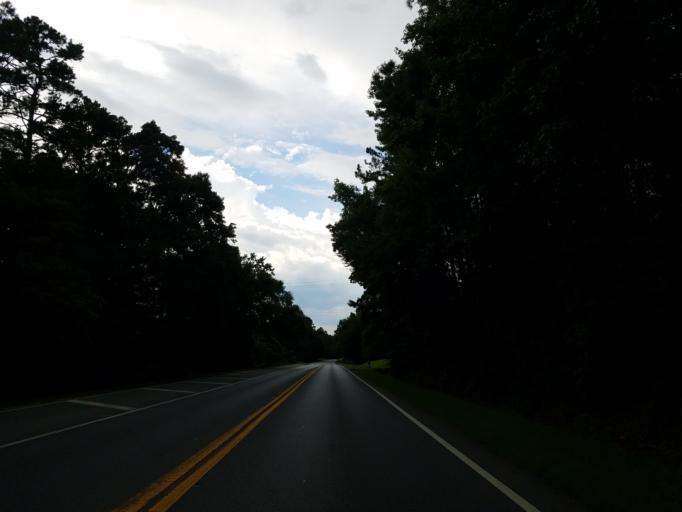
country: US
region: Georgia
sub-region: Bartow County
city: Adairsville
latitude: 34.3529
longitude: -84.9180
